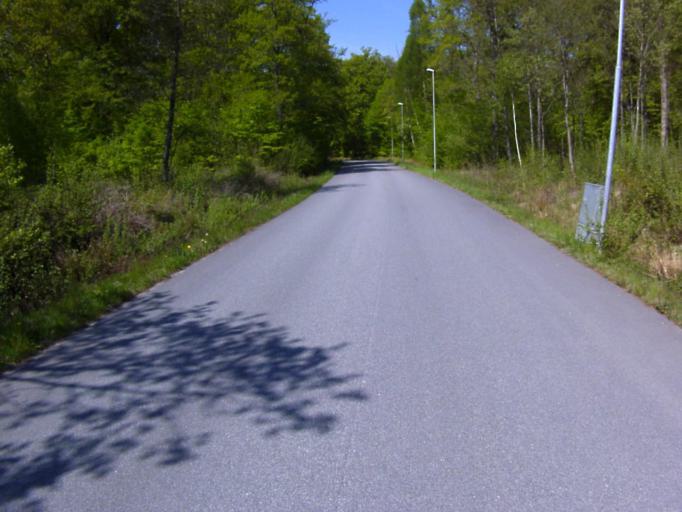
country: SE
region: Skane
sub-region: Kristianstads Kommun
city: Tollarp
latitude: 56.1741
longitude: 14.2992
